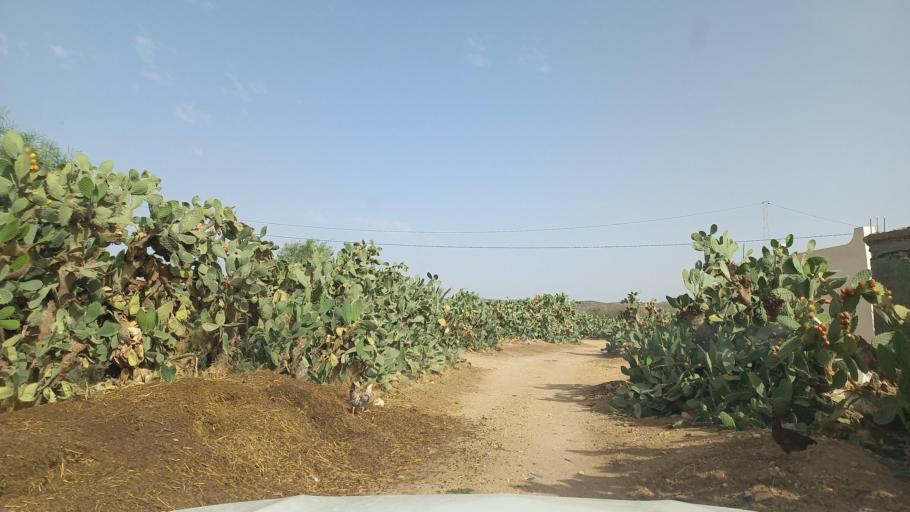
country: TN
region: Al Qasrayn
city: Kasserine
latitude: 35.2988
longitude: 8.9623
